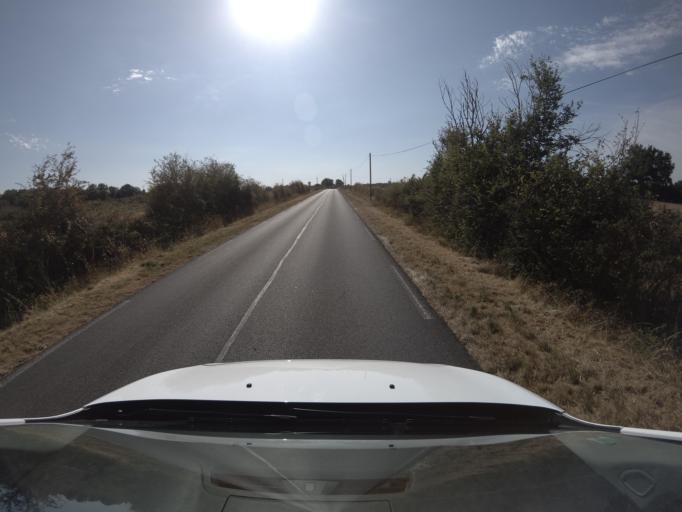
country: FR
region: Poitou-Charentes
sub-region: Departement des Deux-Sevres
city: Argenton-les-Vallees
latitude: 47.0002
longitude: -0.3965
